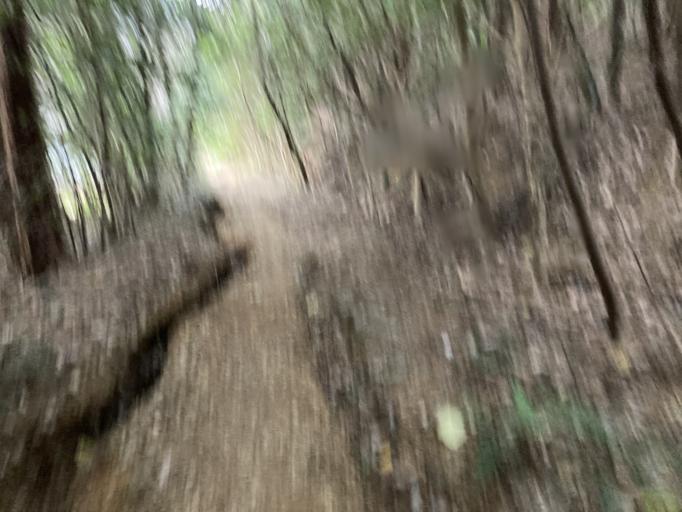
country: JP
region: Aichi
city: Tahara
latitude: 34.6108
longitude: 137.1475
